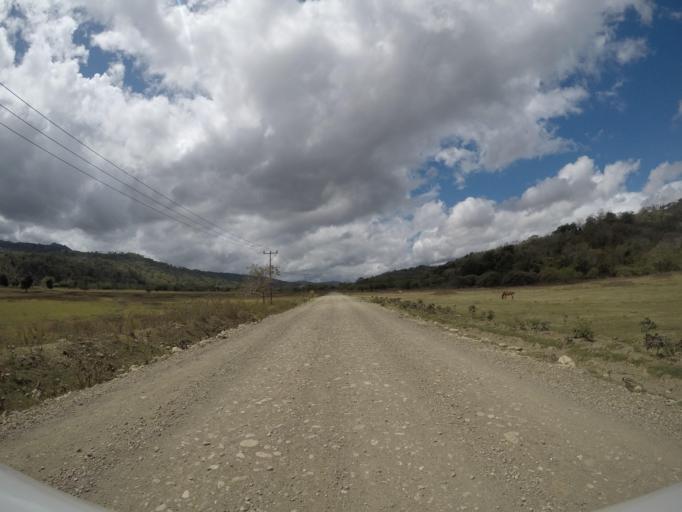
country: TL
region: Lautem
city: Lospalos
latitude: -8.4899
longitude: 126.8215
